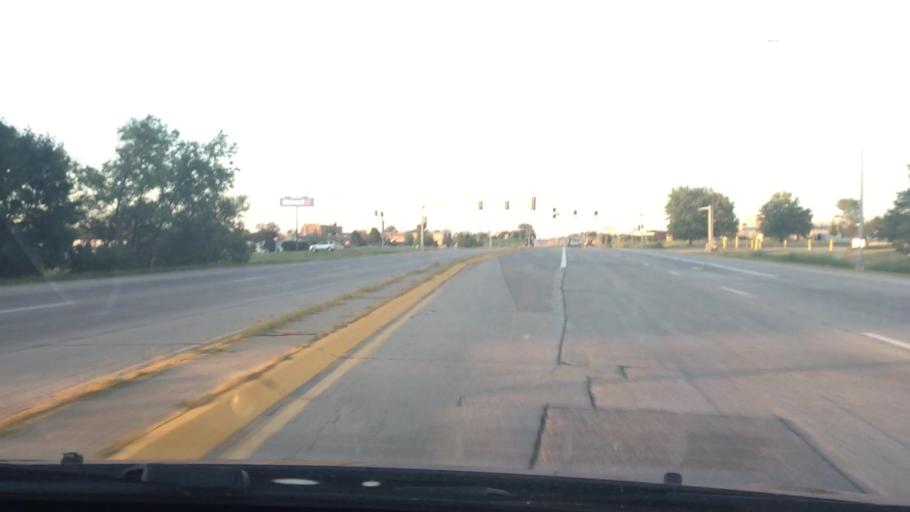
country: US
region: Iowa
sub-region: Muscatine County
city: Muscatine
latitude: 41.4553
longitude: -91.0257
